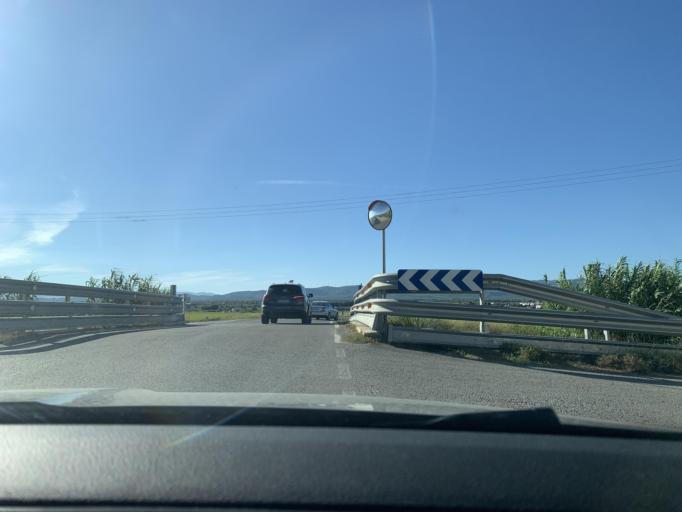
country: ES
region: Catalonia
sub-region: Provincia de Tarragona
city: Camarles
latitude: 40.7760
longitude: 0.6897
